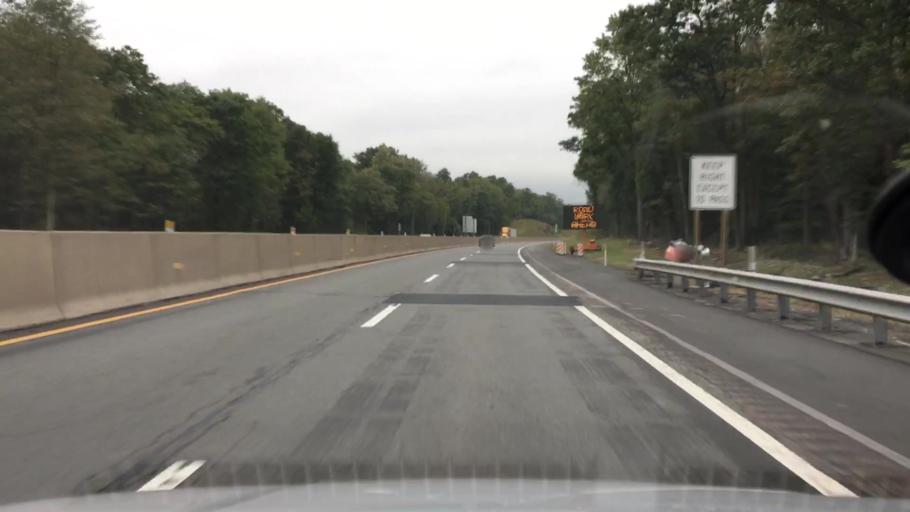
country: US
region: Pennsylvania
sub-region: Luzerne County
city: White Haven
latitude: 41.0832
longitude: -75.7354
